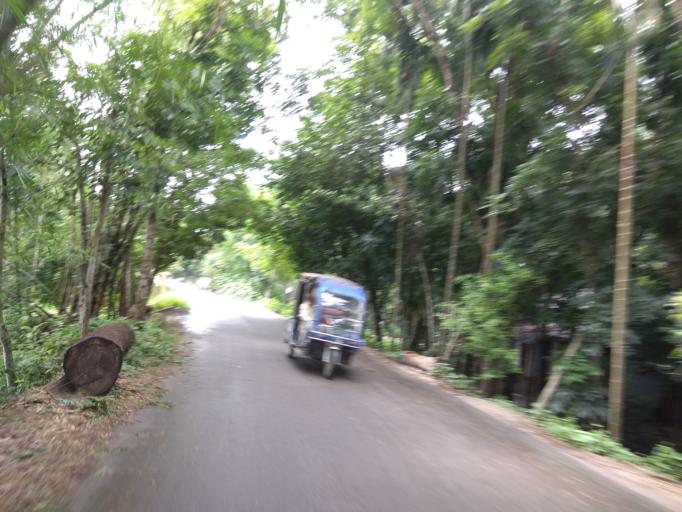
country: BD
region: Dhaka
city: Dohar
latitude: 23.4217
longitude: 90.0649
